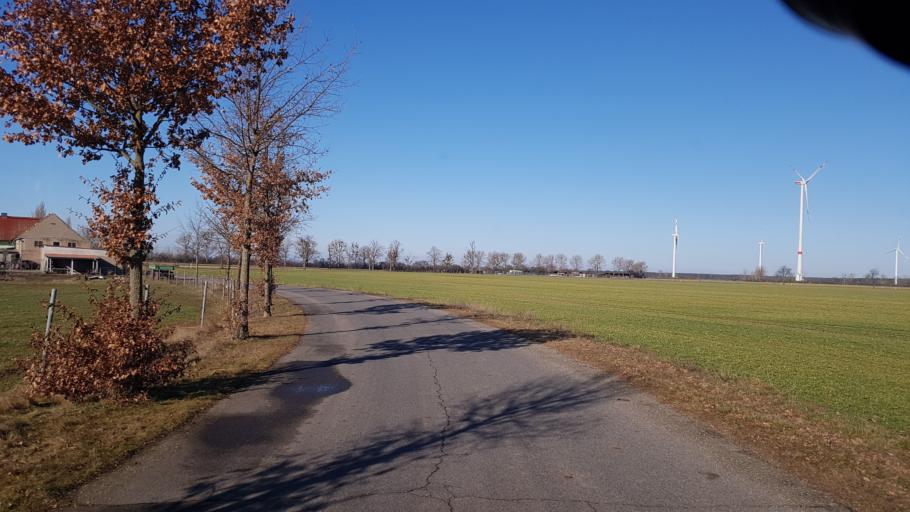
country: DE
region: Brandenburg
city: Muhlberg
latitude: 51.5083
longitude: 13.2293
